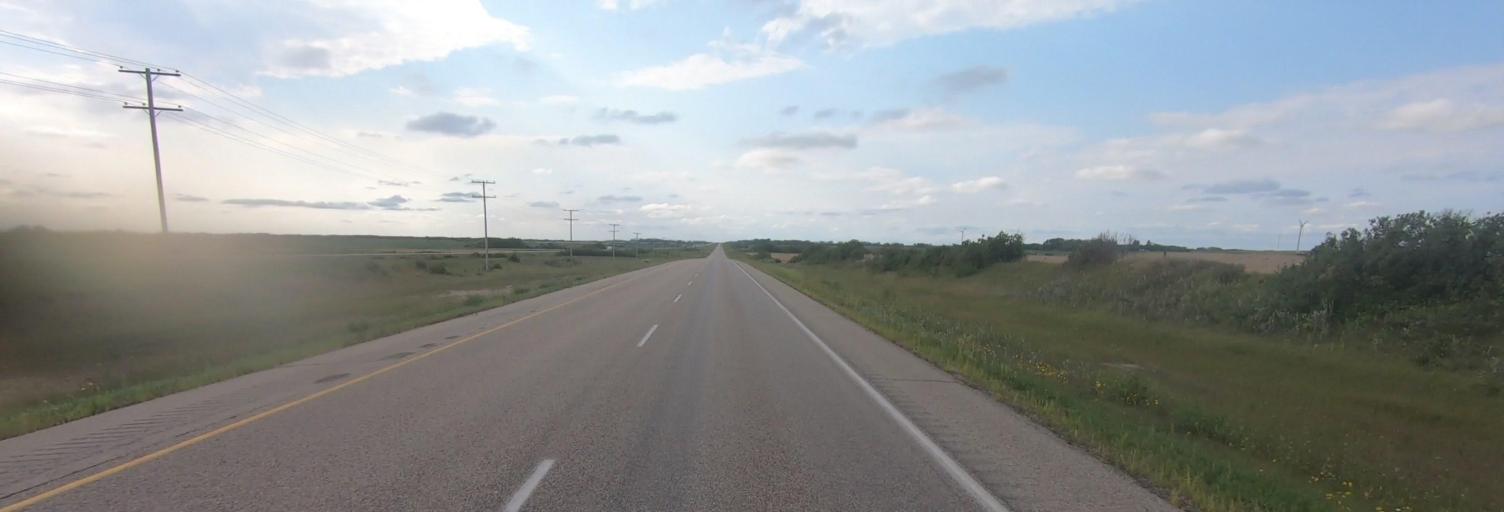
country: CA
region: Saskatchewan
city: Moosomin
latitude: 50.2137
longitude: -101.8047
